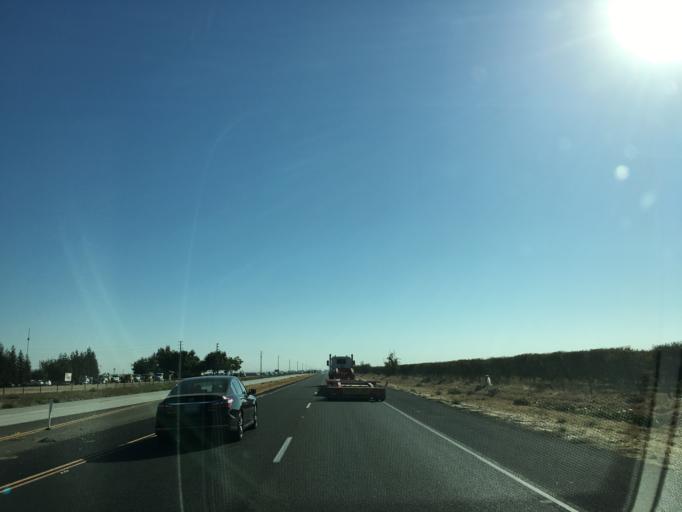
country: US
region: California
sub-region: Madera County
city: Chowchilla
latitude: 37.0837
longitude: -120.2557
